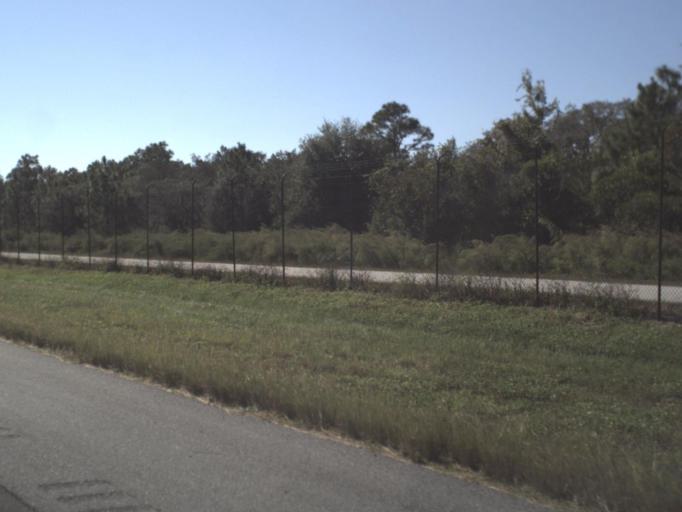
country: US
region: Florida
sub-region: Pasco County
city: Shady Hills
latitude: 28.2986
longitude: -82.5505
